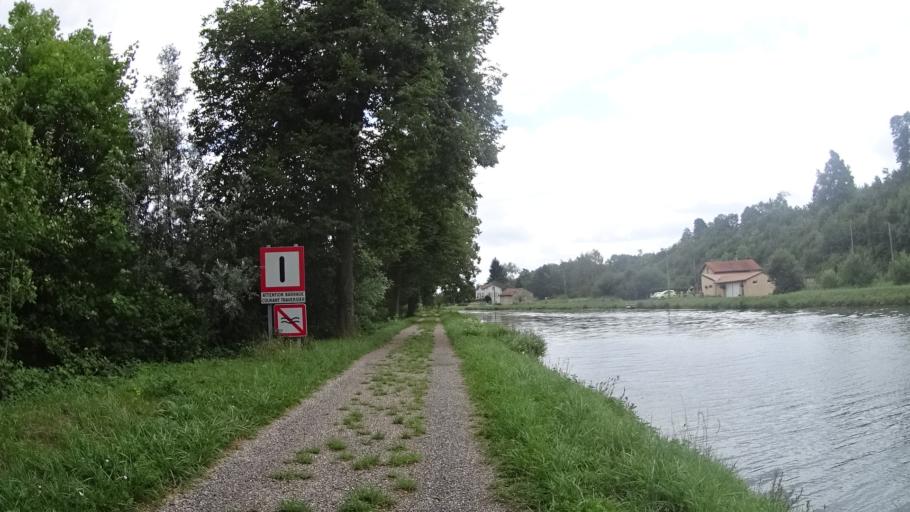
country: FR
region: Lorraine
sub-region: Departement de la Meuse
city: Commercy
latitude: 48.7580
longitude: 5.6035
